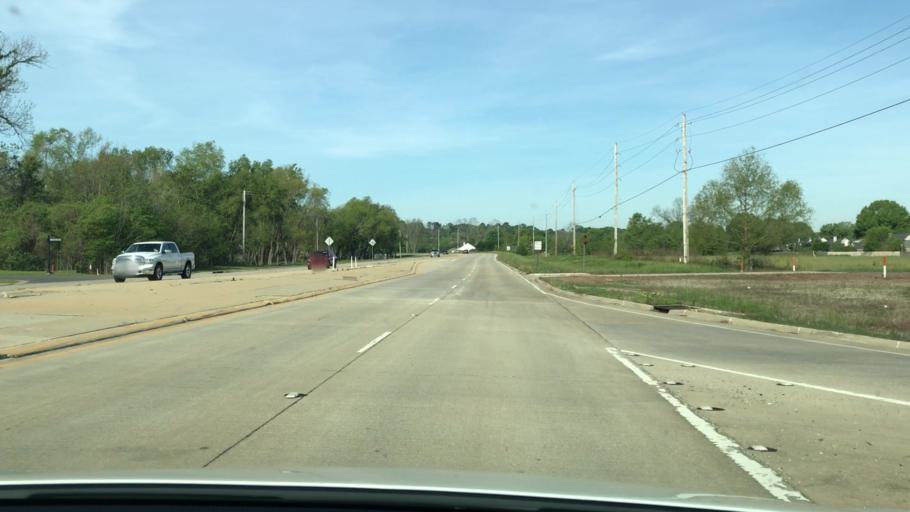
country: US
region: Louisiana
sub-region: Bossier Parish
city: Bossier City
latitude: 32.4004
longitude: -93.7159
